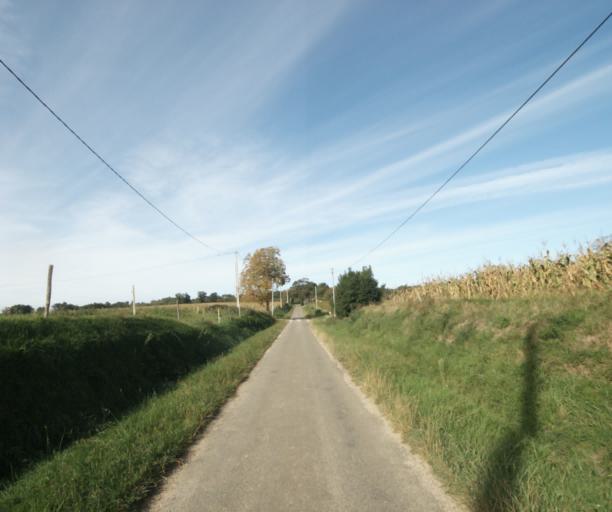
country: FR
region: Midi-Pyrenees
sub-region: Departement du Gers
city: Eauze
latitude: 43.9036
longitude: 0.1274
